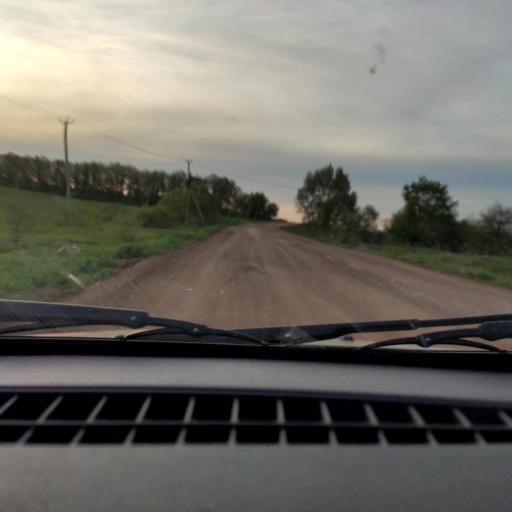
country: RU
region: Bashkortostan
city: Iglino
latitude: 54.8553
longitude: 56.3968
